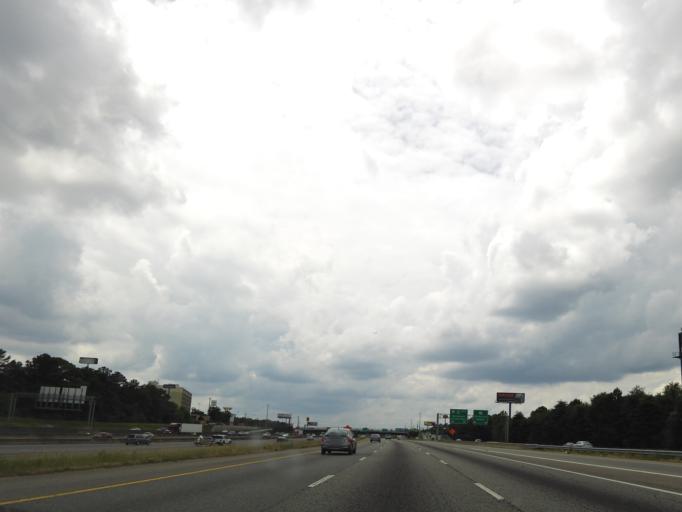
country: US
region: Georgia
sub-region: Fulton County
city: College Park
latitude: 33.6208
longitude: -84.4676
